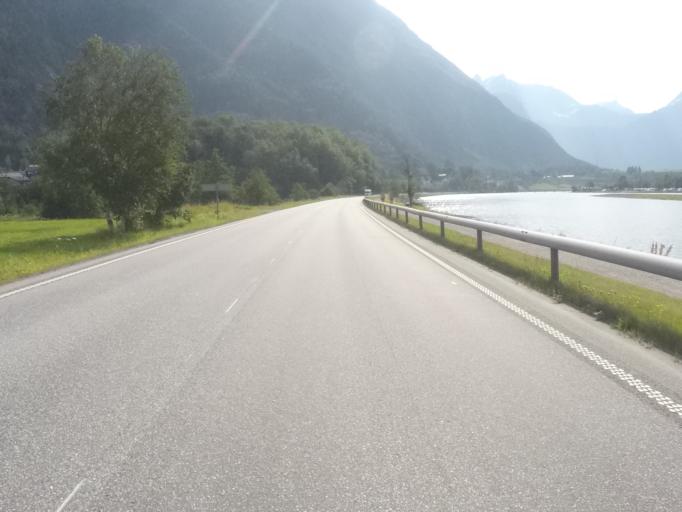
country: NO
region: More og Romsdal
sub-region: Rauma
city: Andalsnes
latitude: 62.5571
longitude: 7.6944
